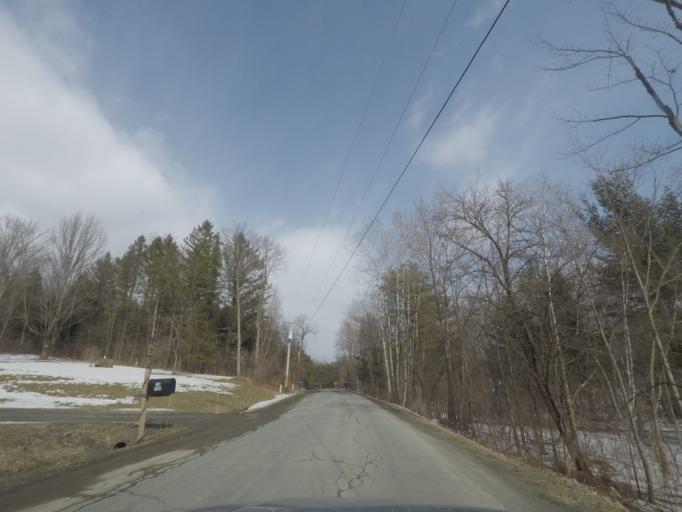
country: US
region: New York
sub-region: Rensselaer County
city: Poestenkill
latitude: 42.7884
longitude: -73.5748
